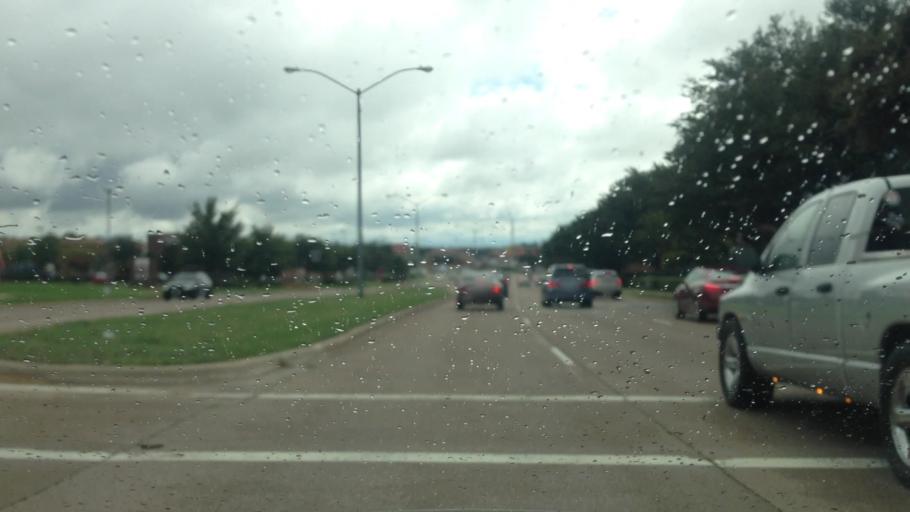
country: US
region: Texas
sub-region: Tarrant County
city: Edgecliff Village
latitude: 32.6668
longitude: -97.4007
